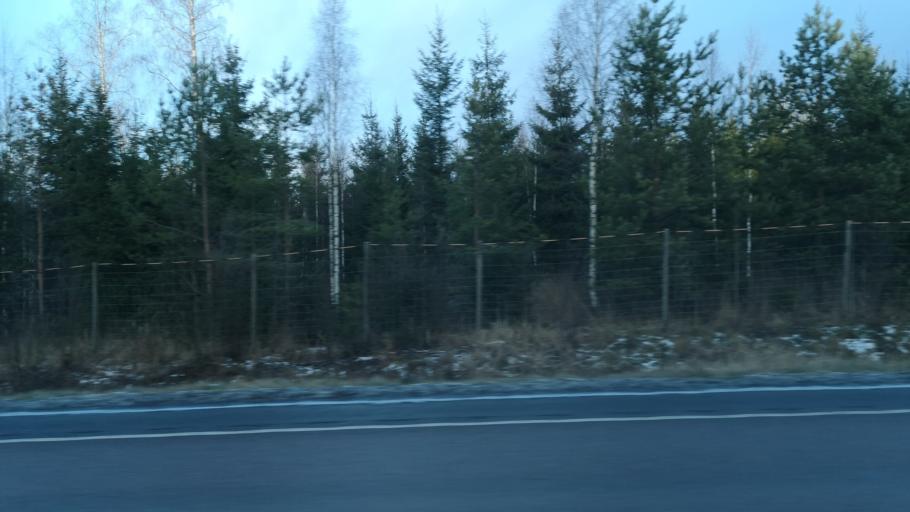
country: FI
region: Southern Savonia
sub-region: Mikkeli
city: Pertunmaa
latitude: 61.3674
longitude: 26.2729
